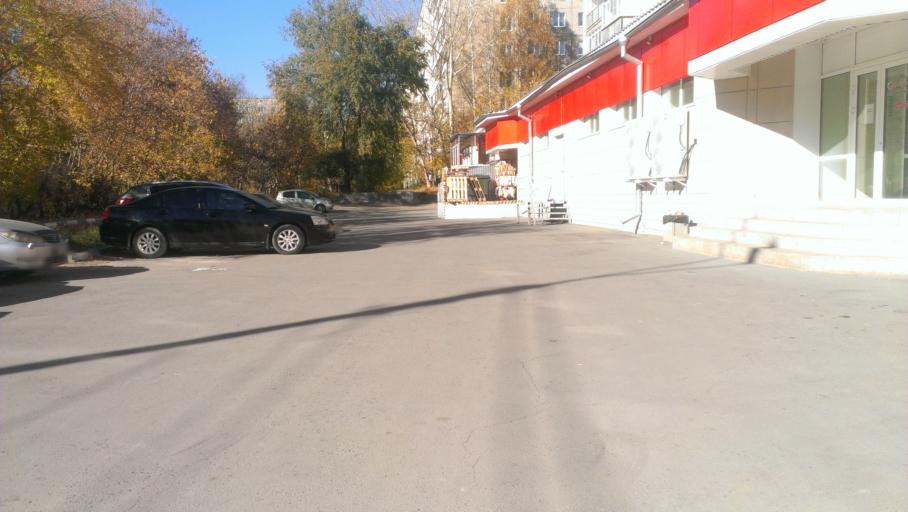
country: RU
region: Altai Krai
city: Novosilikatnyy
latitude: 53.3664
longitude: 83.6672
